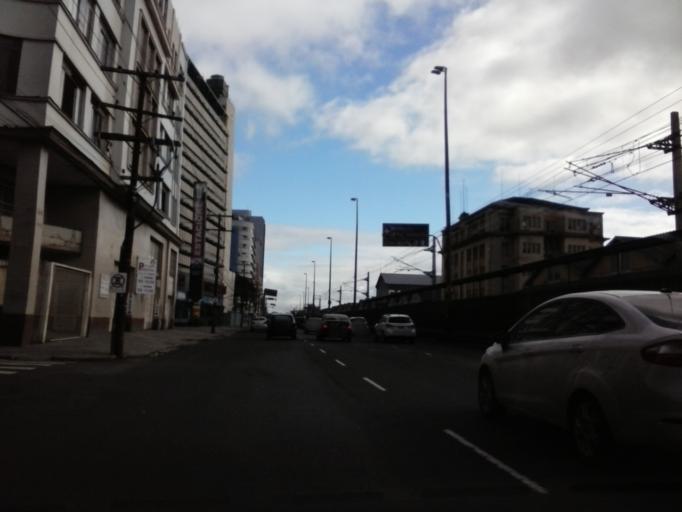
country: BR
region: Rio Grande do Sul
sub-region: Porto Alegre
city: Porto Alegre
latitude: -30.0269
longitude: -51.2300
